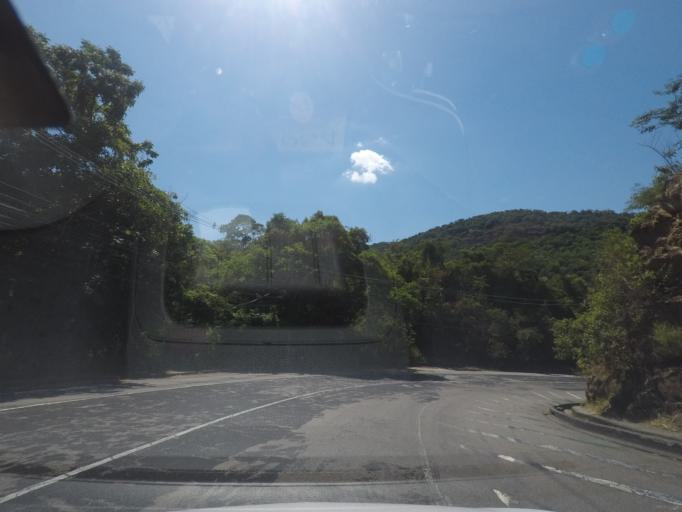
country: BR
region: Rio de Janeiro
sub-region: Niteroi
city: Niteroi
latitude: -22.9257
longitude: -43.0631
